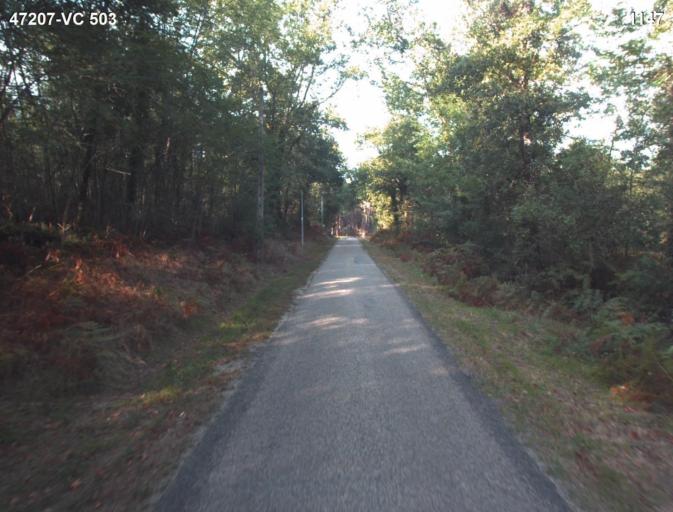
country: FR
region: Aquitaine
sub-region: Departement du Lot-et-Garonne
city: Barbaste
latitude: 44.1966
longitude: 0.2318
